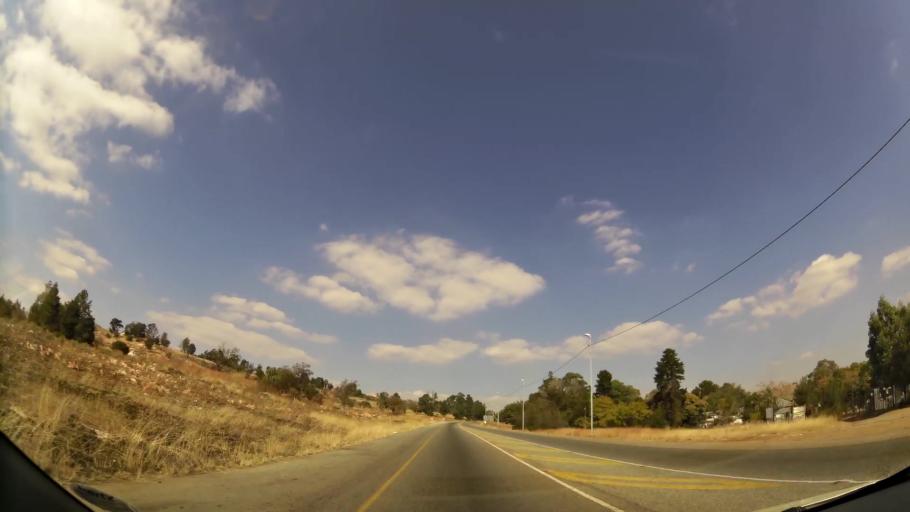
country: ZA
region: Gauteng
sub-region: West Rand District Municipality
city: Krugersdorp
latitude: -26.0368
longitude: 27.7403
